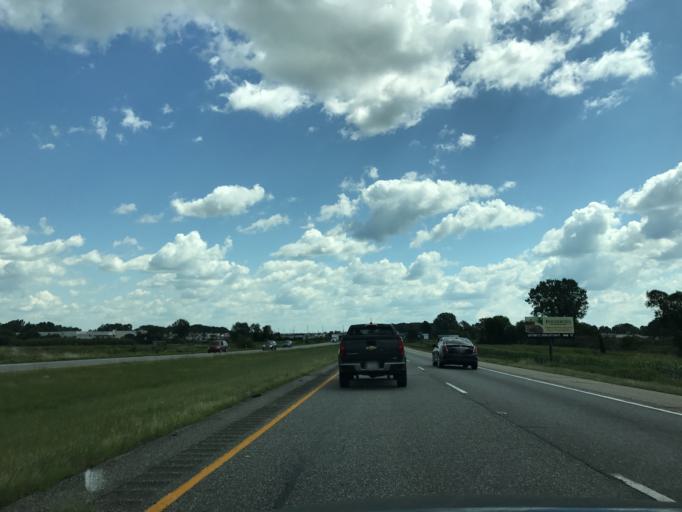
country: US
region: Indiana
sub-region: Marshall County
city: Plymouth
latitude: 41.3614
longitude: -86.3385
